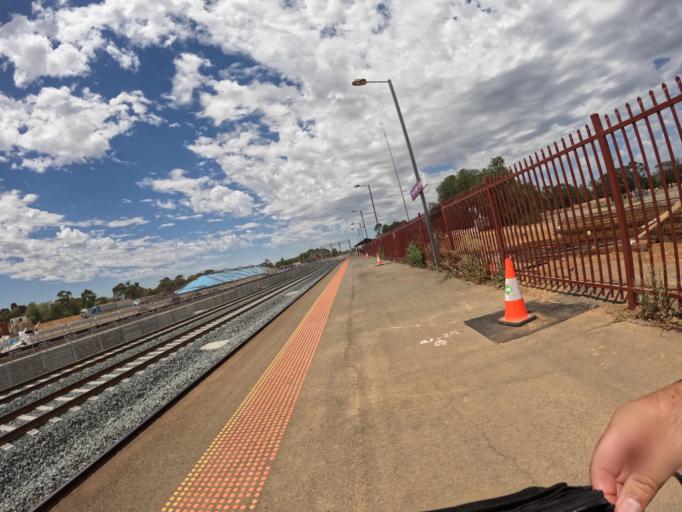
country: AU
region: Victoria
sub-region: Greater Shepparton
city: Shepparton
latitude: -36.6124
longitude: 145.2406
